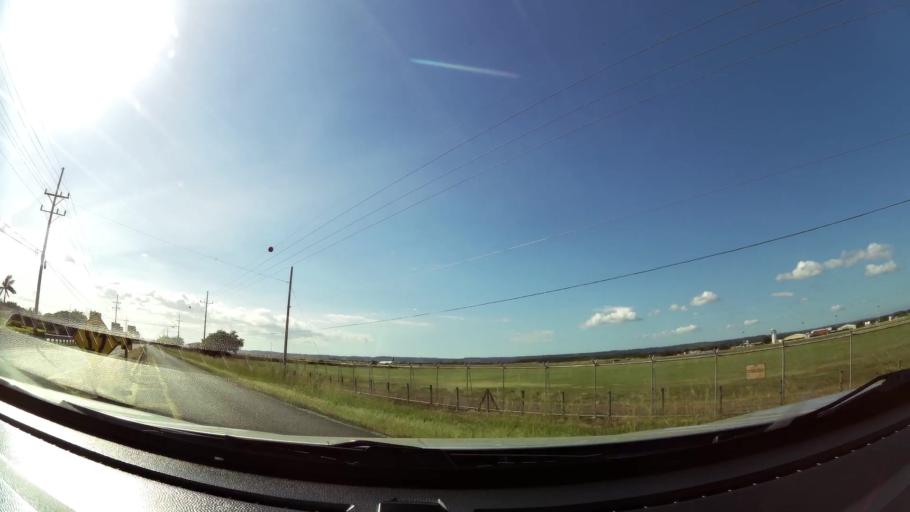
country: CR
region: Guanacaste
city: Liberia
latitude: 10.5935
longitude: -85.5358
